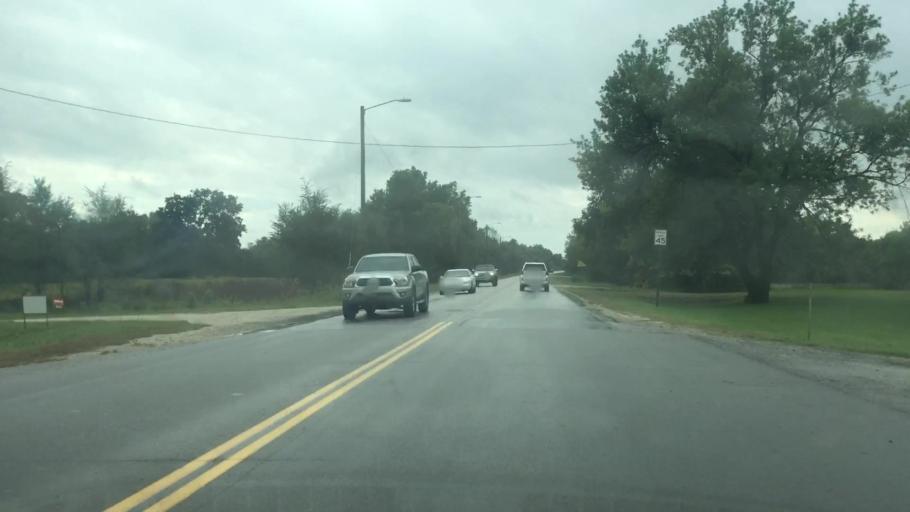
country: US
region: Kansas
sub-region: Allen County
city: Iola
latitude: 37.9144
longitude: -95.4091
